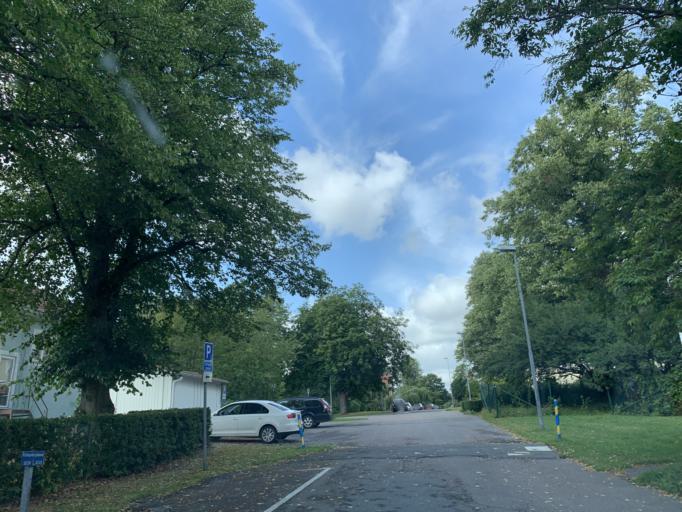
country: SE
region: Vaestra Goetaland
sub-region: Goteborg
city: Eriksbo
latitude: 57.7418
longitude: 12.0630
